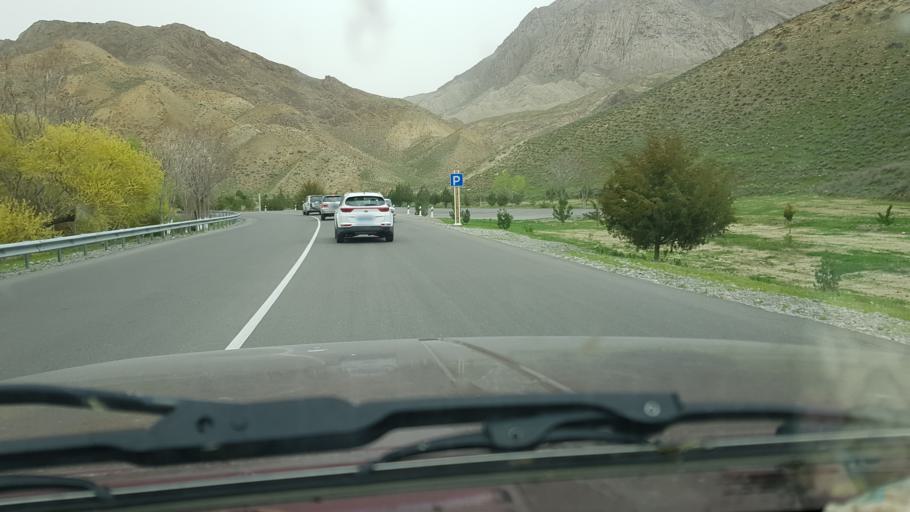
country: TM
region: Ahal
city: Arcabil
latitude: 38.0081
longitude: 58.0075
